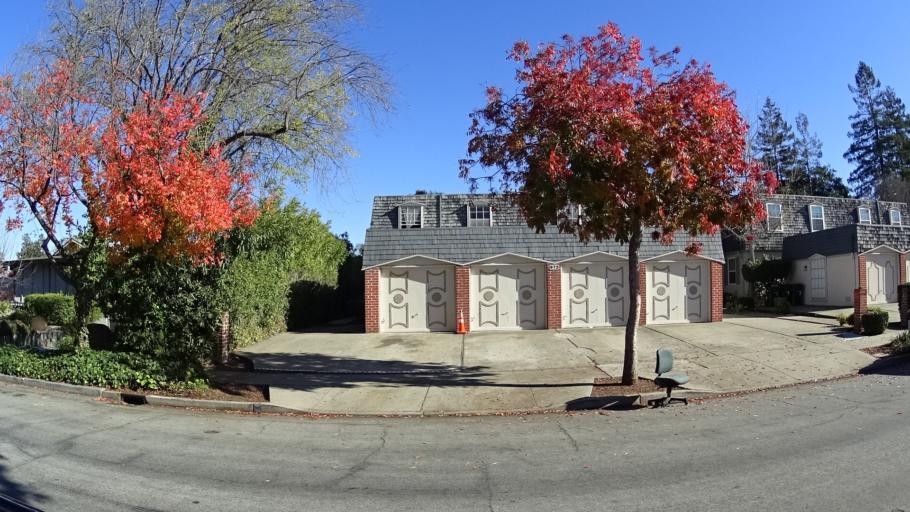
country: US
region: California
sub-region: Santa Clara County
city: Sunnyvale
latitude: 37.3571
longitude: -122.0119
